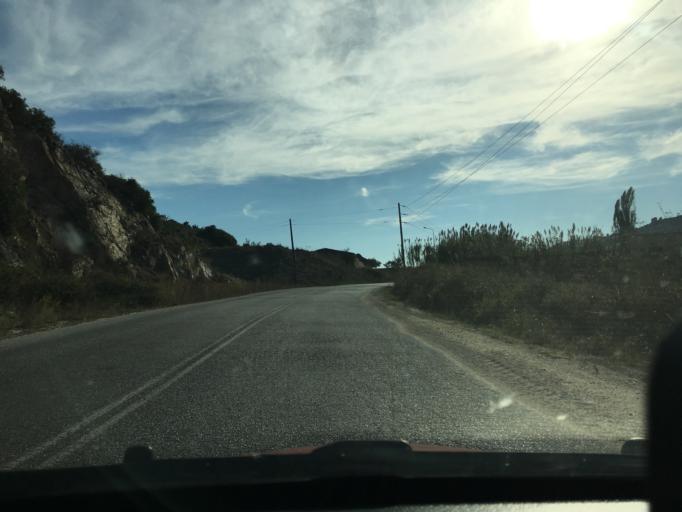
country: GR
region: Central Macedonia
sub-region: Nomos Chalkidikis
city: Agios Nikolaos
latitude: 40.2475
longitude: 23.7116
